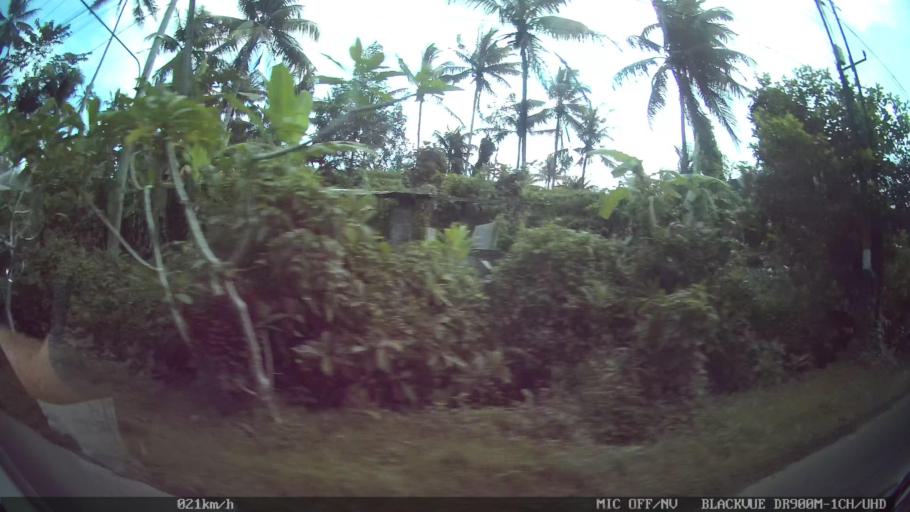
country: ID
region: Bali
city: Banjar Pesalakan
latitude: -8.4886
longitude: 115.2980
